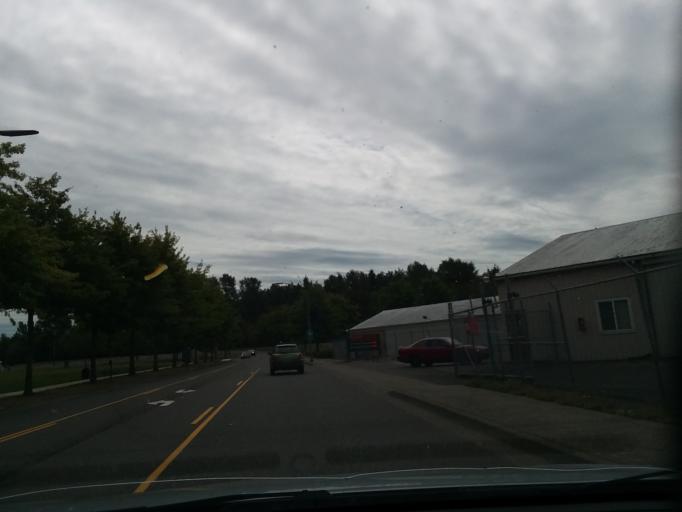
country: US
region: Washington
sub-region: Whatcom County
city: Marietta-Alderwood
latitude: 48.7910
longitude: -122.5306
